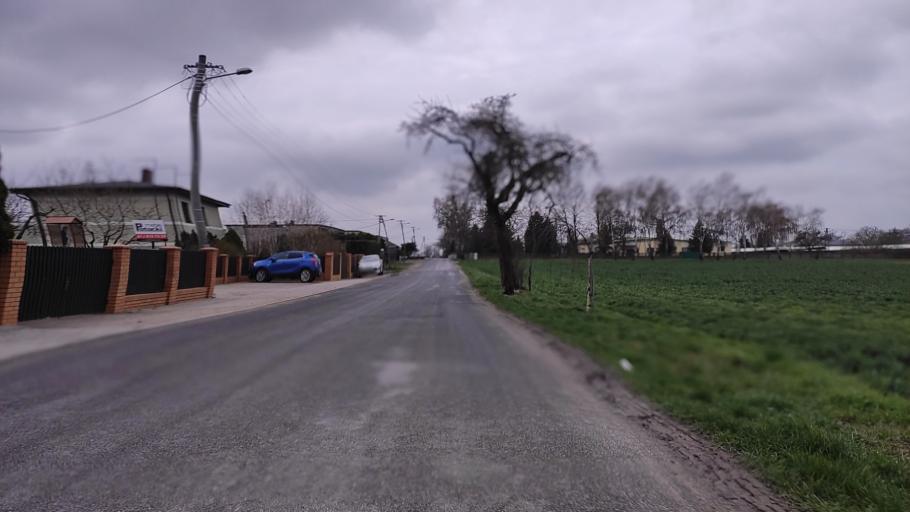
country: PL
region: Greater Poland Voivodeship
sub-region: Powiat poznanski
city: Kostrzyn
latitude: 52.4045
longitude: 17.1646
